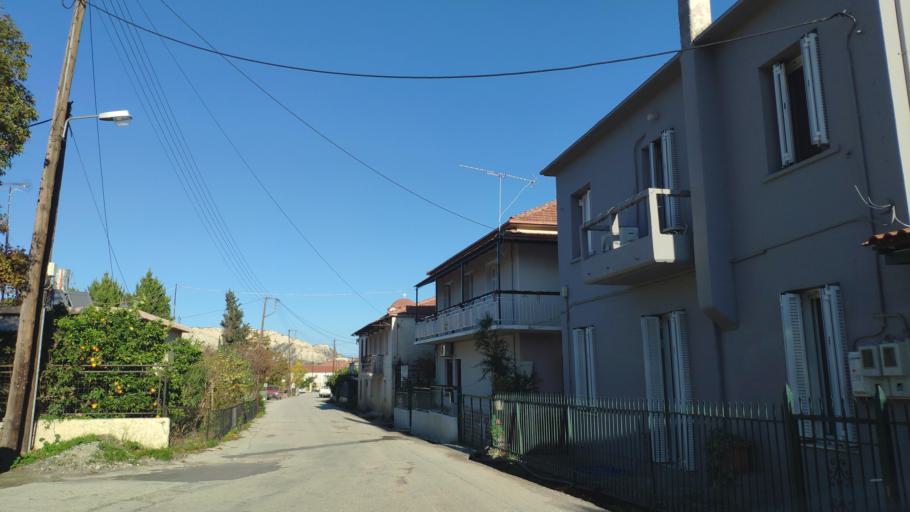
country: GR
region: Peloponnese
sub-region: Nomos Korinthias
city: Xylokastro
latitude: 38.0447
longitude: 22.5850
